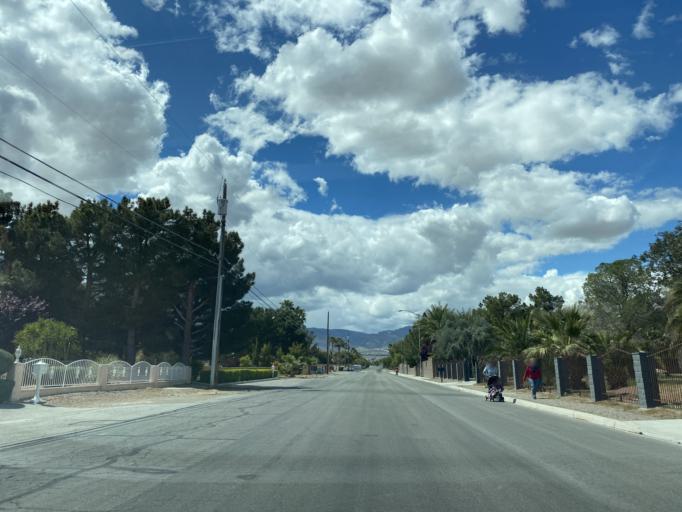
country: US
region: Nevada
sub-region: Clark County
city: Spring Valley
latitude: 36.2444
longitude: -115.2674
